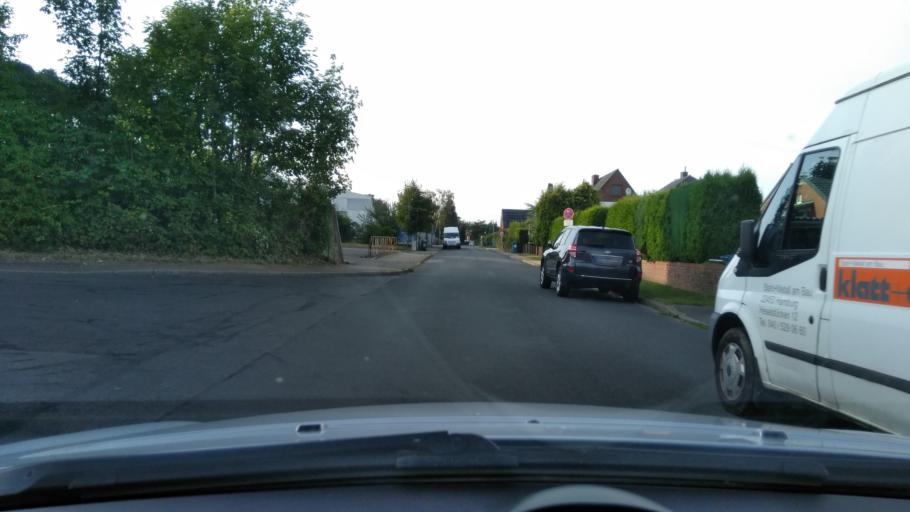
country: DE
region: Schleswig-Holstein
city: Barsbuettel
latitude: 53.5660
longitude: 10.1786
